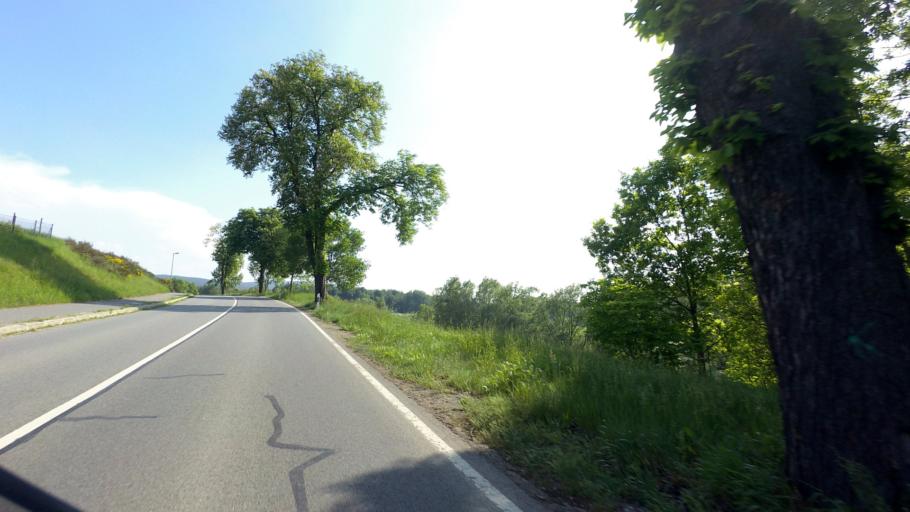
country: DE
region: Saxony
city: Grosspostwitz
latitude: 51.1096
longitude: 14.4567
